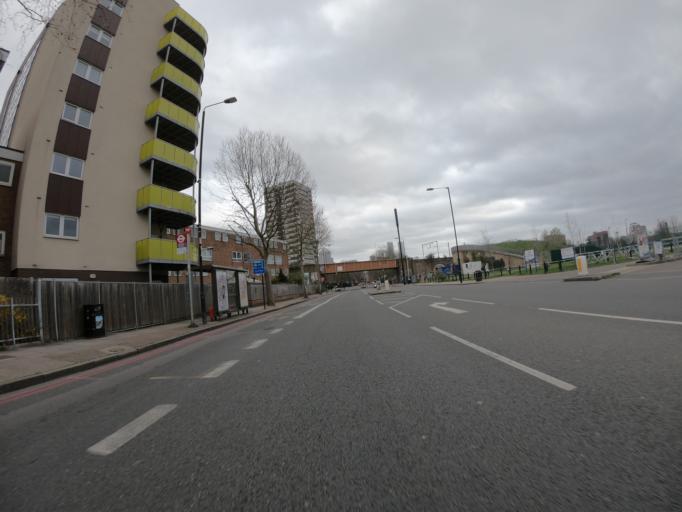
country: GB
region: England
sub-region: Greater London
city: Poplar
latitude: 51.5194
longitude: -0.0309
